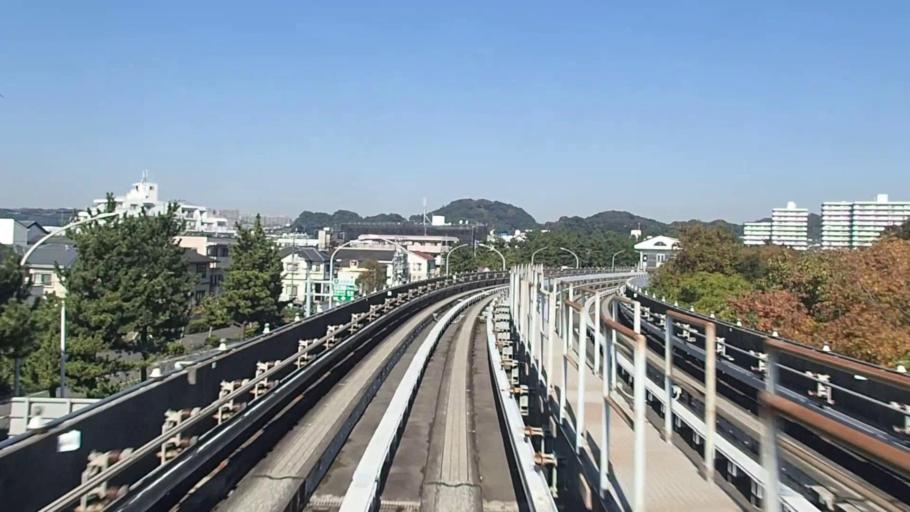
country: JP
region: Kanagawa
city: Yokosuka
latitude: 35.3361
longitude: 139.6320
